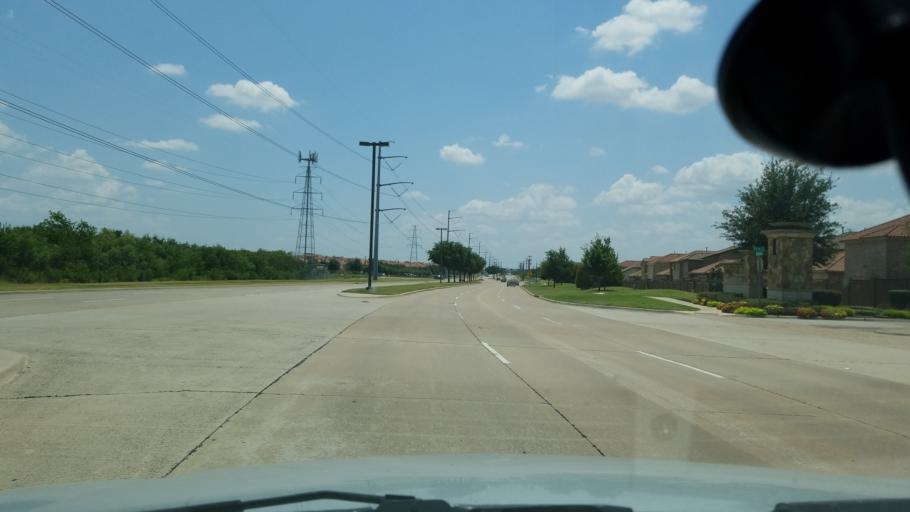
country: US
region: Texas
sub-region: Dallas County
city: Farmers Branch
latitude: 32.9056
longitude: -96.9426
